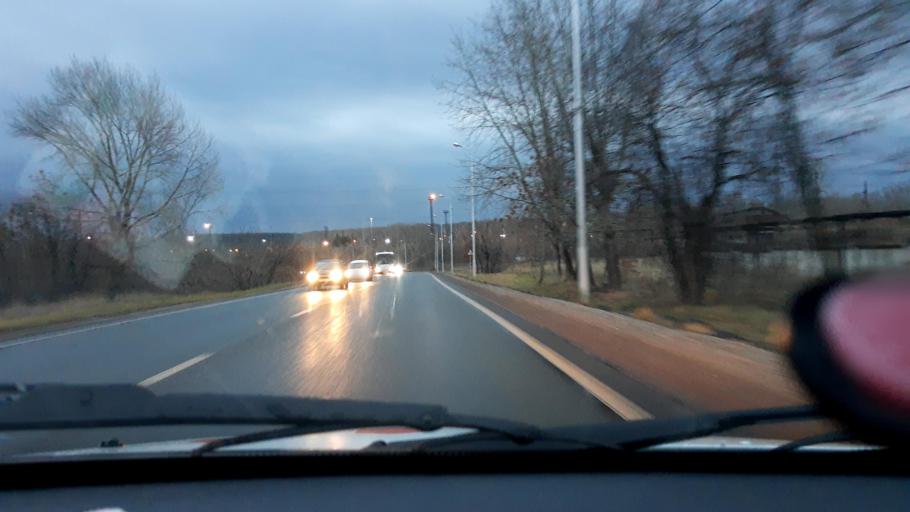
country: RU
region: Bashkortostan
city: Ufa
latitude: 54.8420
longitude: 56.1227
